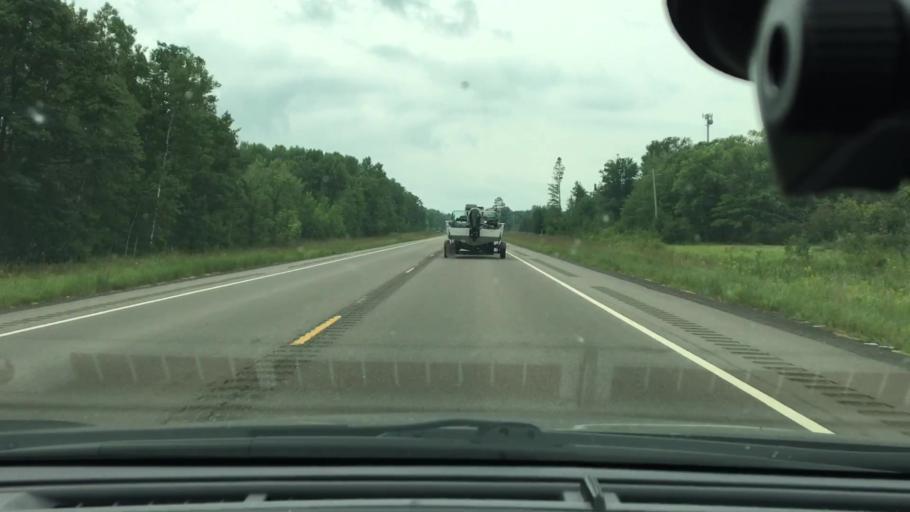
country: US
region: Minnesota
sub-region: Crow Wing County
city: Crosby
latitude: 46.5830
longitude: -93.9527
